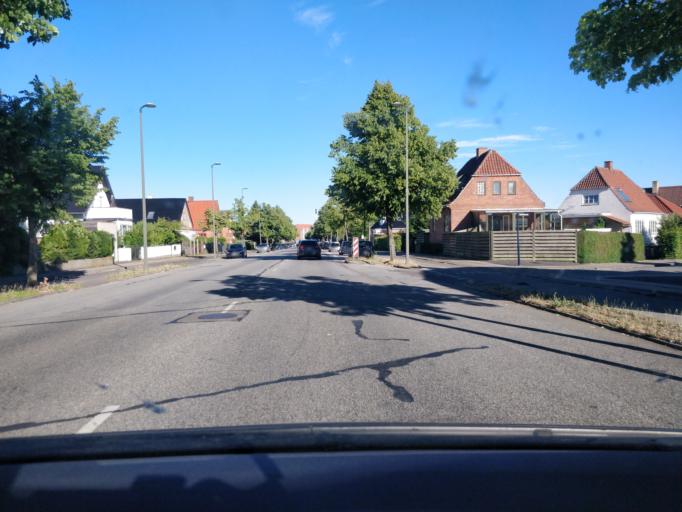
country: DK
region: Capital Region
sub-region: Kobenhavn
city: Vanlose
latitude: 55.6959
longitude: 12.4889
